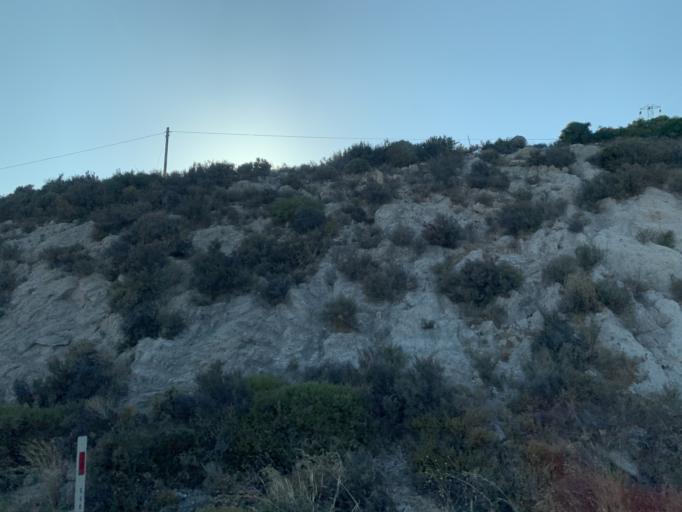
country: TR
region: Izmir
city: Alacati
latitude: 38.2835
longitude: 26.4025
